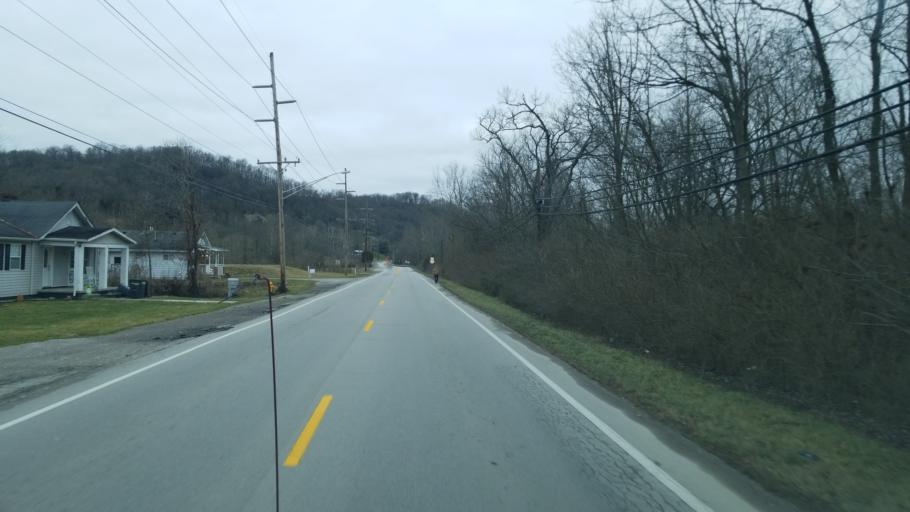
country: US
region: Kentucky
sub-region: Campbell County
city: Silver Grove
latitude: 39.0425
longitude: -84.4152
